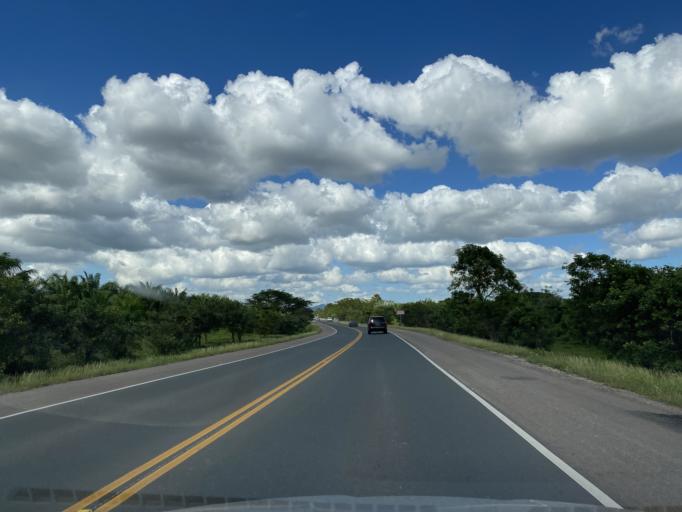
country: DO
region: Monte Plata
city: Monte Plata
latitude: 18.7291
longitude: -69.7609
